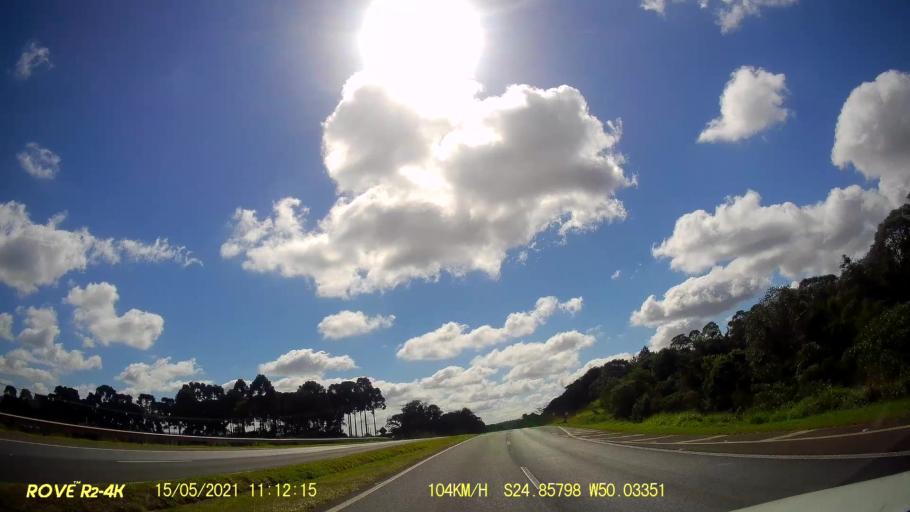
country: BR
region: Parana
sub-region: Castro
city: Castro
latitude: -24.8577
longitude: -50.0339
